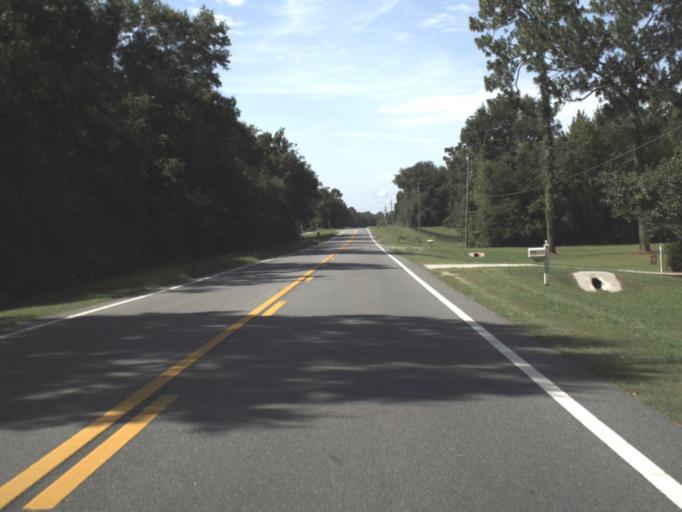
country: US
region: Florida
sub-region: Madison County
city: Madison
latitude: 30.5410
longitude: -83.3675
